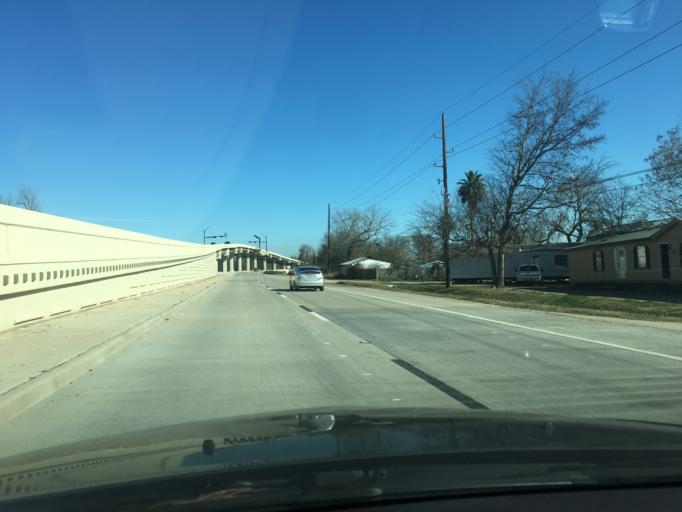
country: US
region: Texas
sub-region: Fort Bend County
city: Richmond
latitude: 29.5923
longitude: -95.7445
